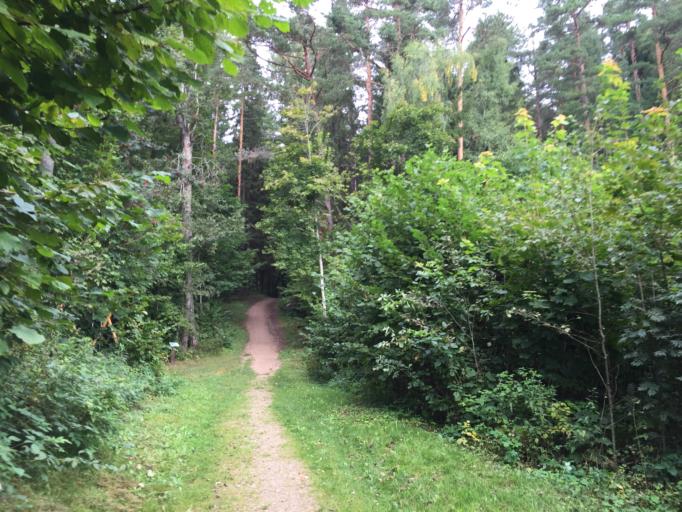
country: LV
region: Dagda
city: Dagda
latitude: 56.2677
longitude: 27.6559
